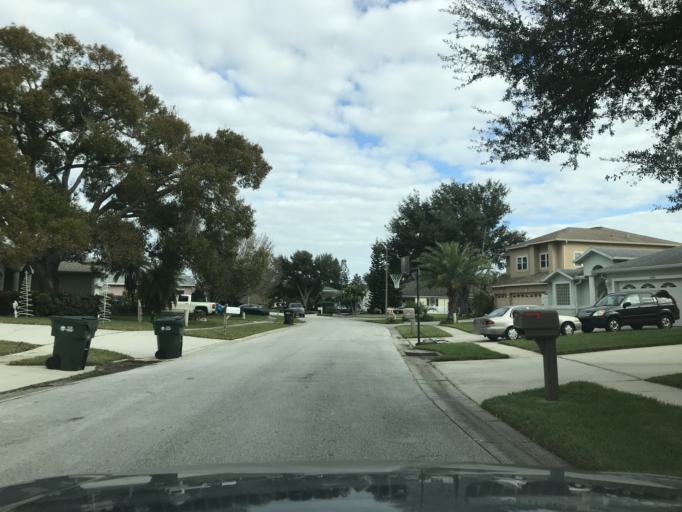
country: US
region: Florida
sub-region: Pinellas County
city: Largo
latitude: 27.9287
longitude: -82.7787
